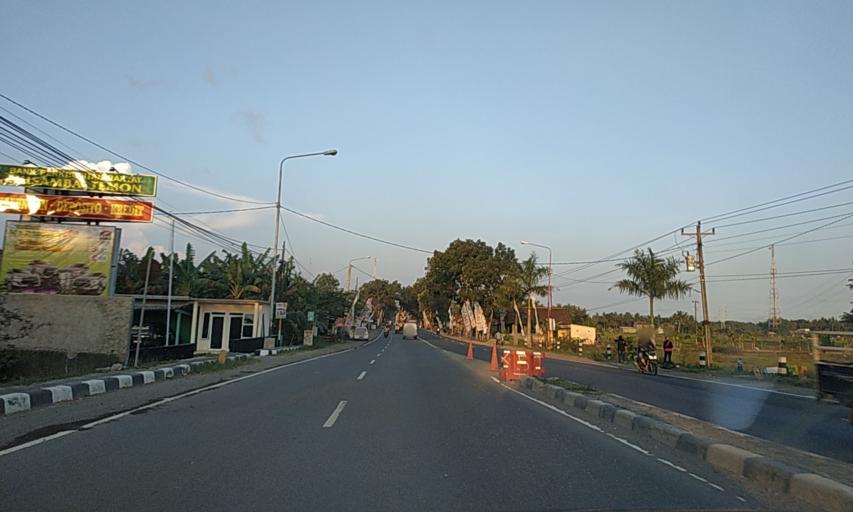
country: ID
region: Daerah Istimewa Yogyakarta
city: Srandakan
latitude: -7.8866
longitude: 110.0724
